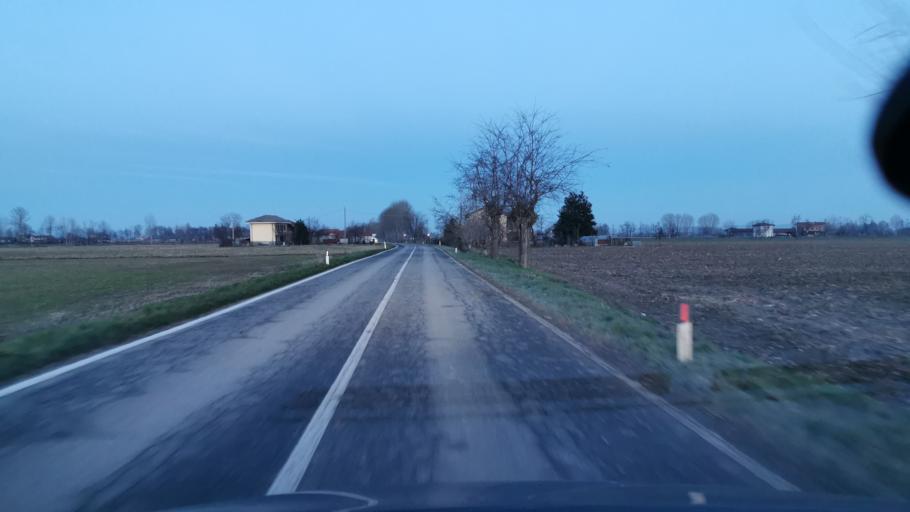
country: IT
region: Piedmont
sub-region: Provincia di Cuneo
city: Caraglio
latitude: 44.4463
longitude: 7.4724
